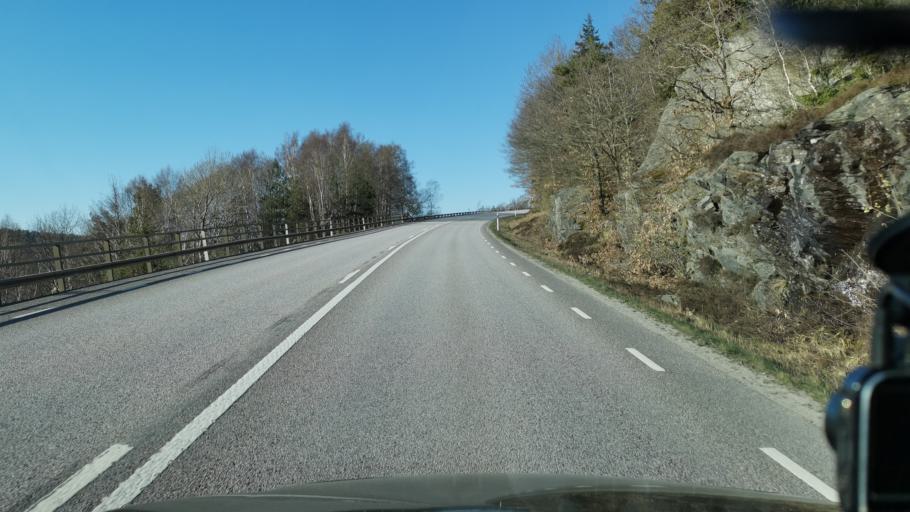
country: SE
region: Vaestra Goetaland
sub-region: Orust
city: Henan
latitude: 58.2588
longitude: 11.6780
